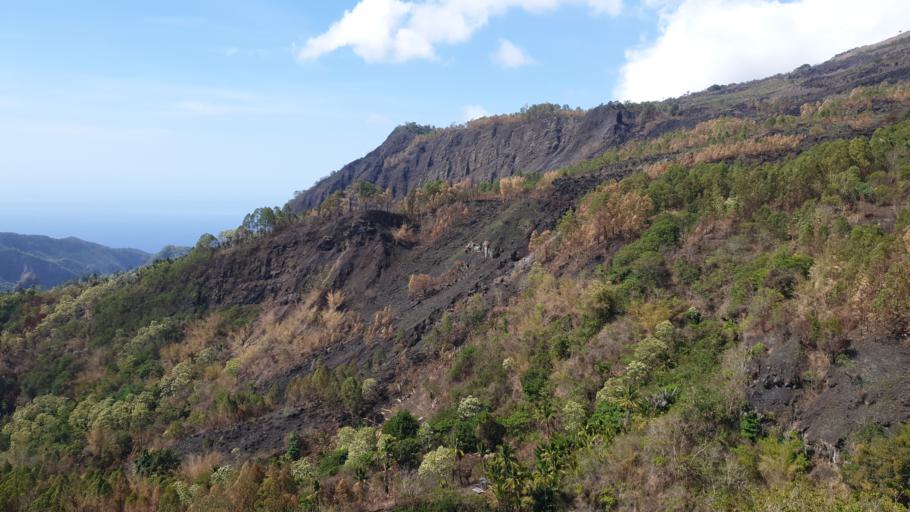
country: ID
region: East Nusa Tenggara
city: Gurusina
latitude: -8.8786
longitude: 120.9855
